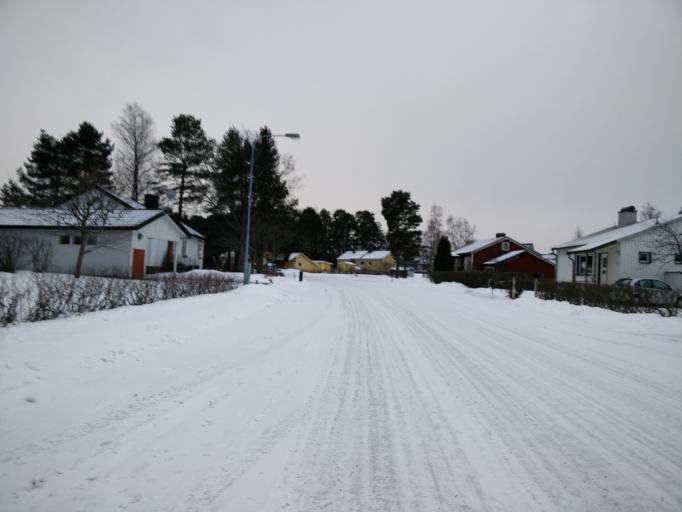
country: SE
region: Vaesternorrland
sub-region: Sundsvalls Kommun
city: Nolby
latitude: 62.2896
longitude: 17.3623
